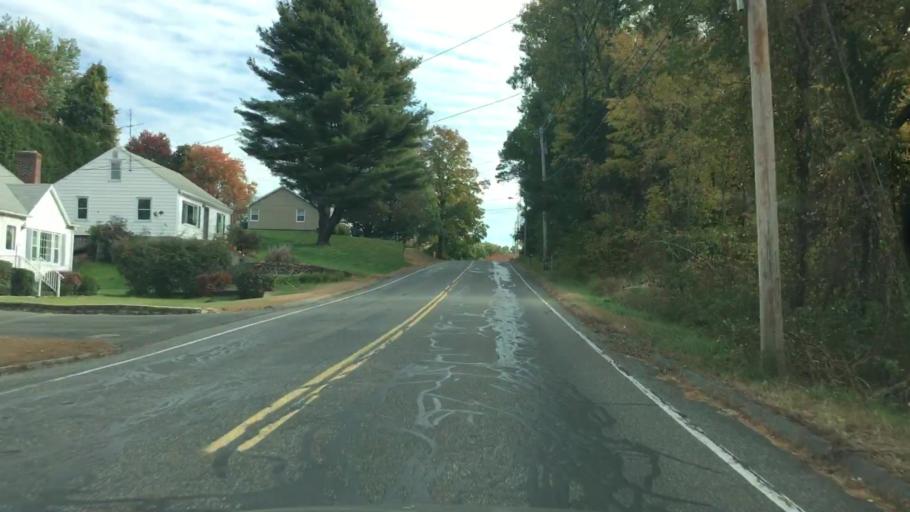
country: US
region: Massachusetts
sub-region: Hampden County
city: East Longmeadow
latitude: 42.0410
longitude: -72.5104
